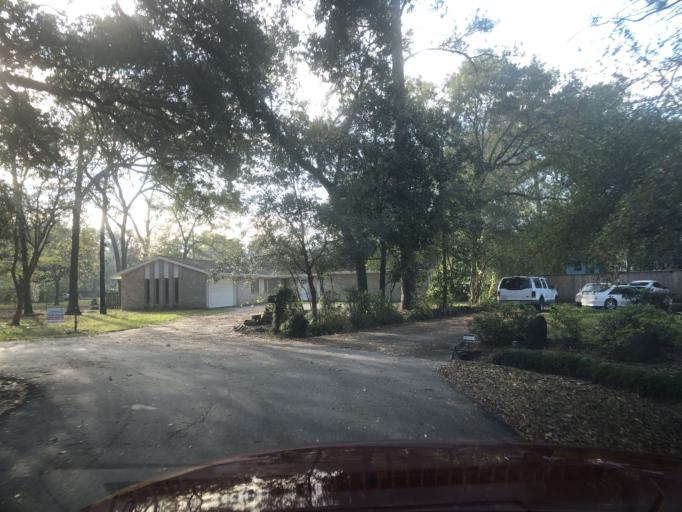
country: US
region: Texas
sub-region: Harris County
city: Spring
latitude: 30.0166
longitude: -95.4746
